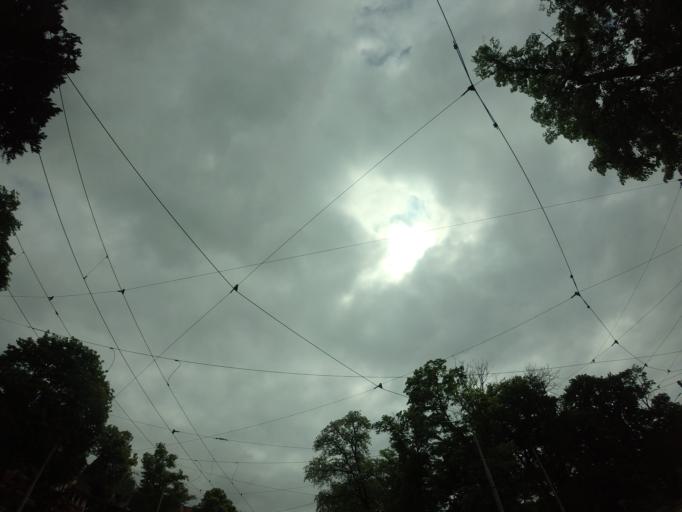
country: PL
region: West Pomeranian Voivodeship
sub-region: Szczecin
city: Szczecin
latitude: 53.4407
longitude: 14.5316
